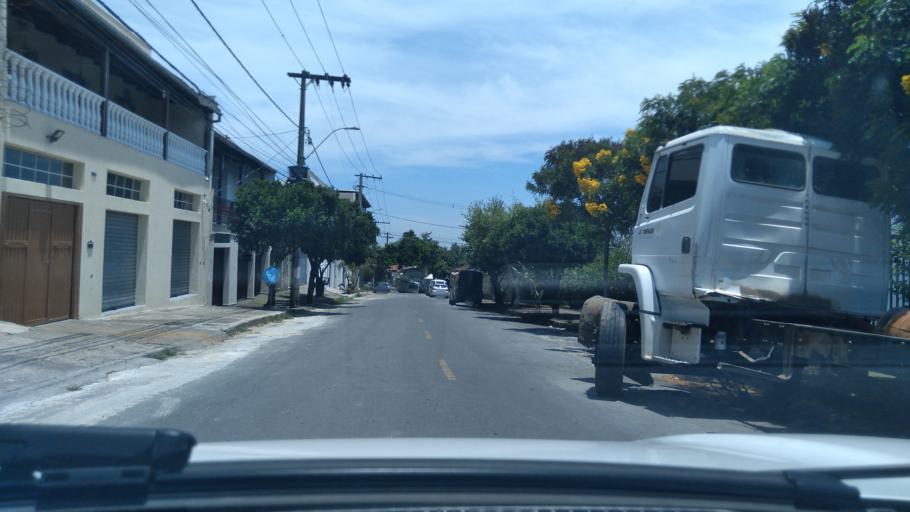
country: BR
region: Minas Gerais
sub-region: Contagem
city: Contagem
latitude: -19.9261
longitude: -44.0152
